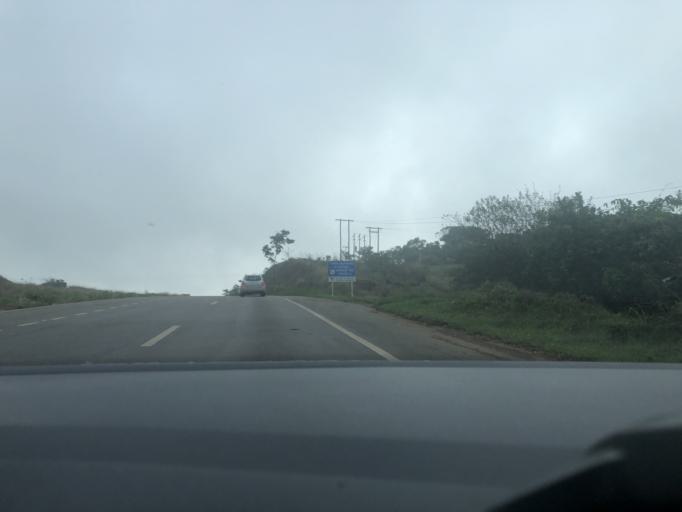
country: BR
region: Minas Gerais
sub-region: Congonhas
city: Congonhas
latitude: -20.5924
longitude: -43.9414
